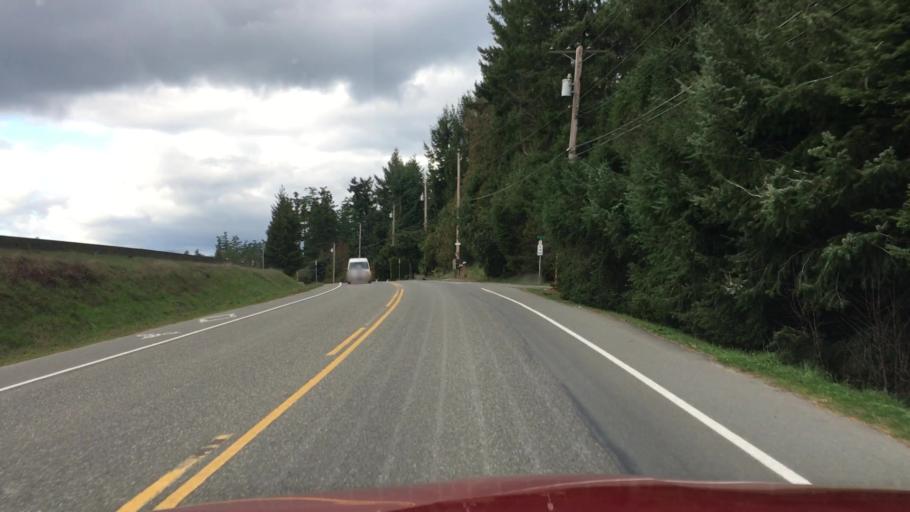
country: CA
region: British Columbia
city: North Saanich
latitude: 48.6055
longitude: -123.3960
